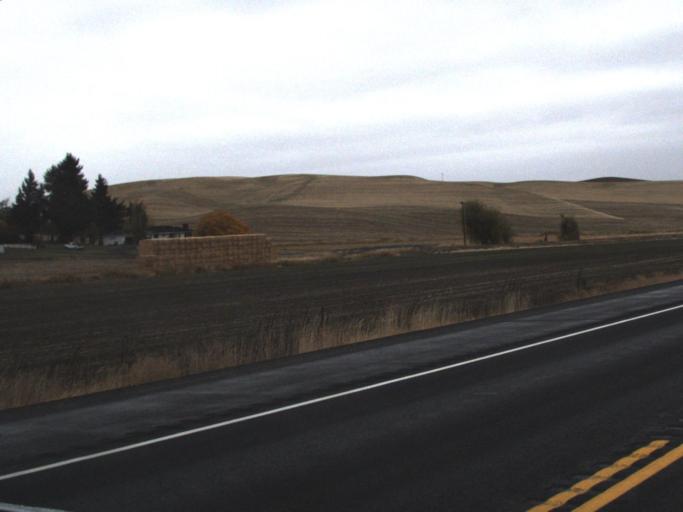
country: US
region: Washington
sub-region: Whitman County
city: Colfax
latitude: 46.8127
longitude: -117.3207
